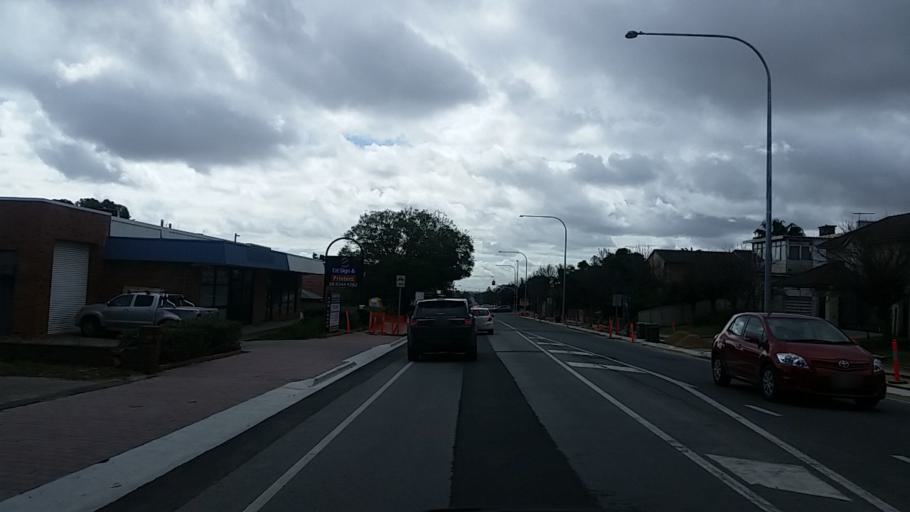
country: AU
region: South Australia
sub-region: Prospect
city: Prospect
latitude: -34.8757
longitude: 138.5932
